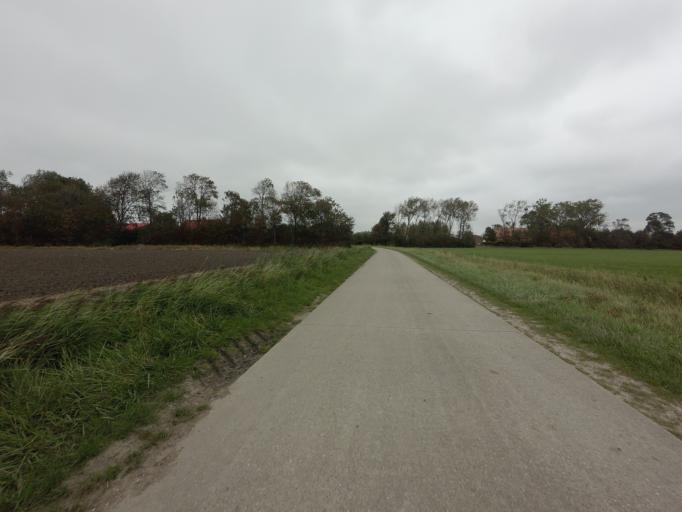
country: NL
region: Zeeland
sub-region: Gemeente Veere
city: Veere
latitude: 51.5259
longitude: 3.6553
